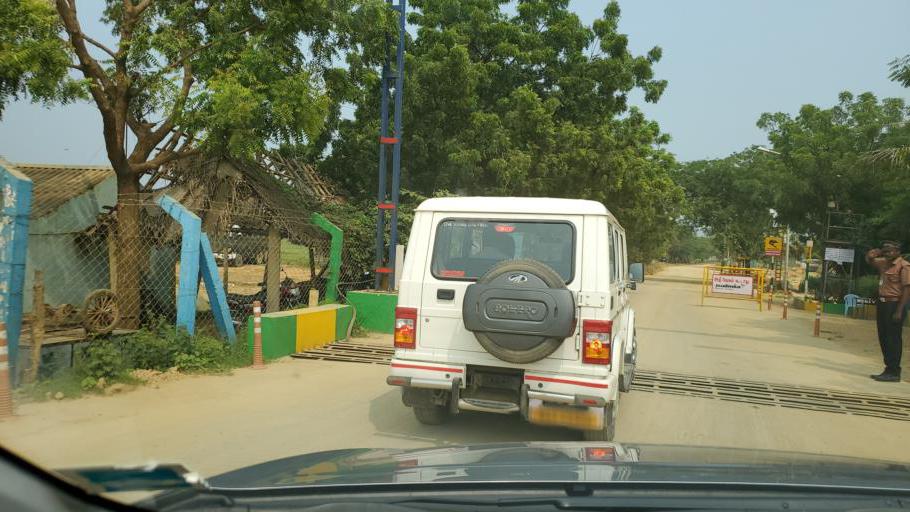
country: IN
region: Tamil Nadu
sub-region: Ariyalur
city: Ariyalur
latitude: 11.1236
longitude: 79.1401
